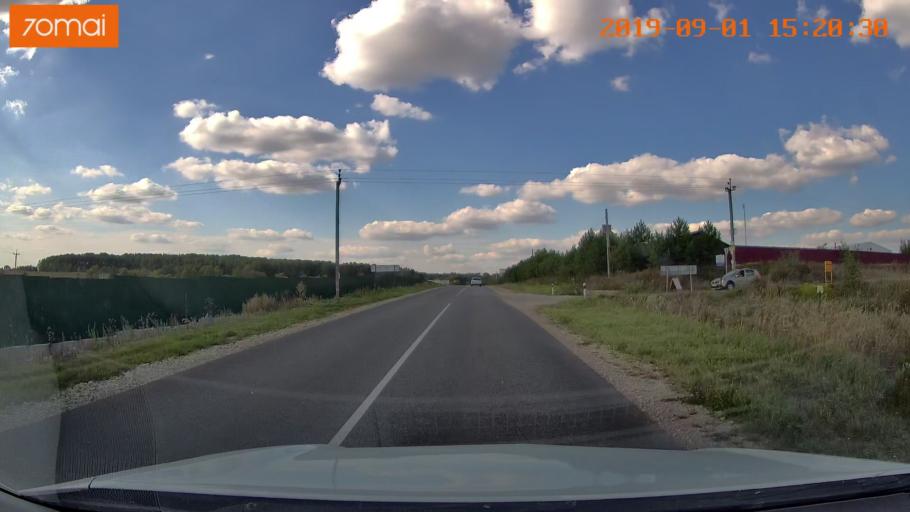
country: RU
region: Kaluga
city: Maloyaroslavets
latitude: 54.9201
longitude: 36.4795
